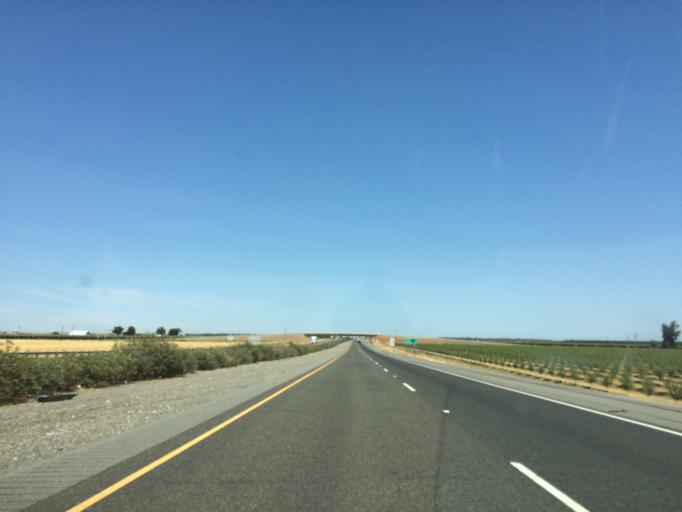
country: US
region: California
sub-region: Glenn County
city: Willows
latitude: 39.5343
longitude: -122.2146
